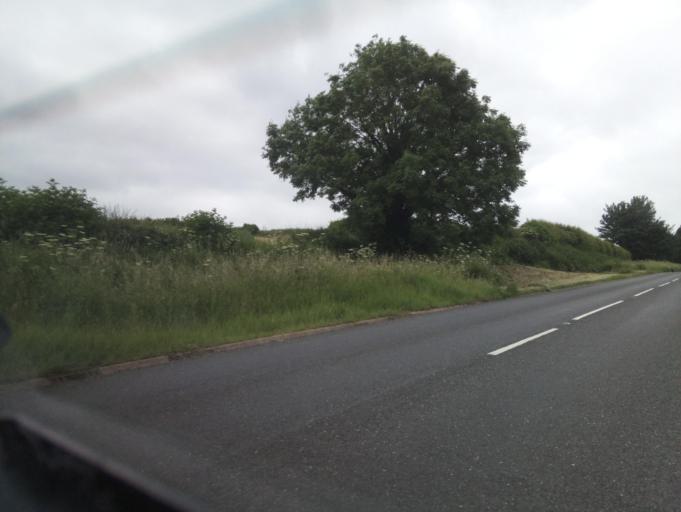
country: GB
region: England
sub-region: District of Rutland
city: Preston
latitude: 52.6183
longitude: -0.7135
